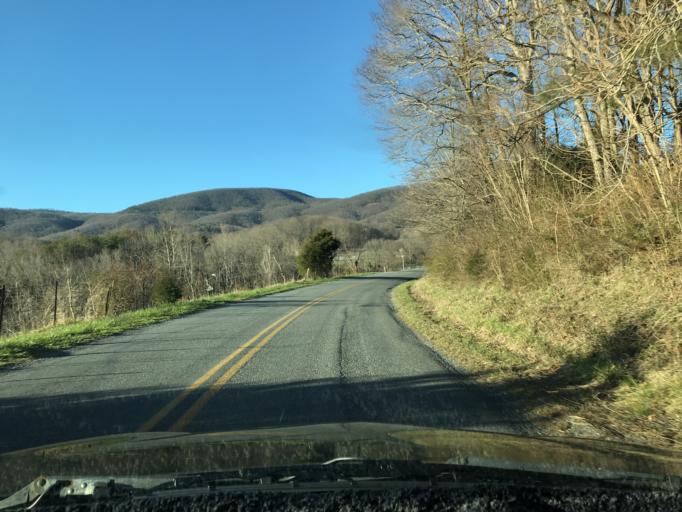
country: US
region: Virginia
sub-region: Botetourt County
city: Buchanan
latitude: 37.4582
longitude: -79.6622
